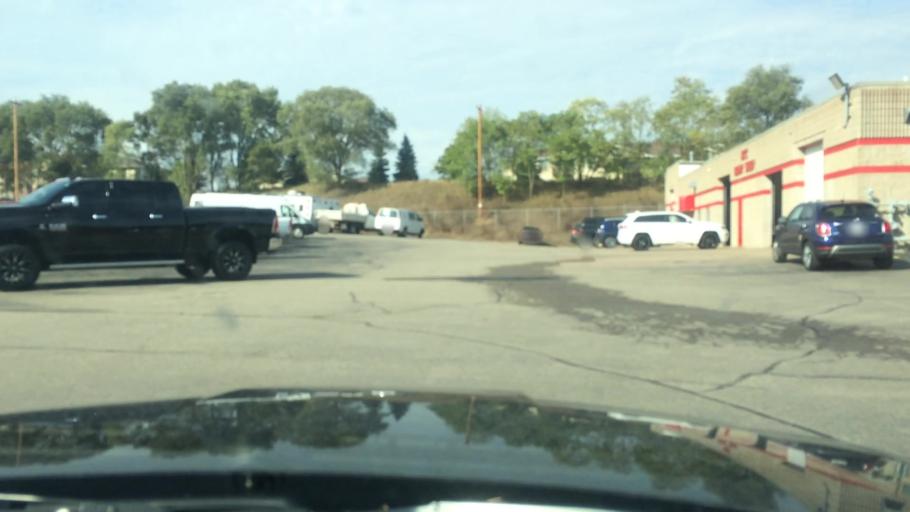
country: US
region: Wisconsin
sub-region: Marathon County
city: Schofield
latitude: 44.9311
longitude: -89.6134
